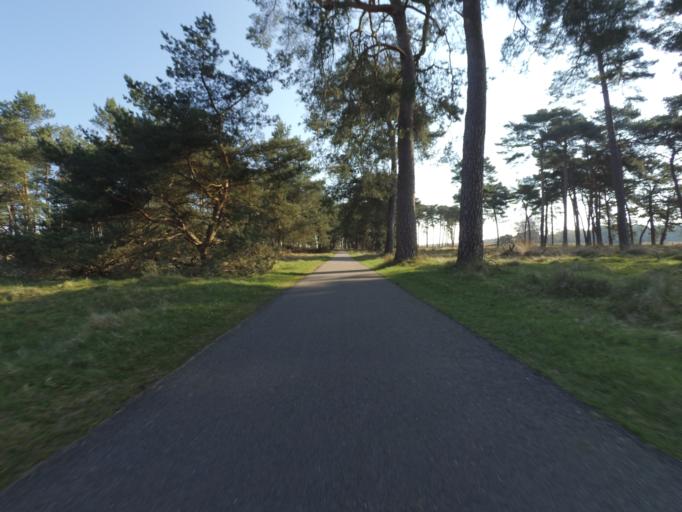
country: NL
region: Gelderland
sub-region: Gemeente Arnhem
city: Hoogkamp
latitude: 52.0735
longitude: 5.8611
